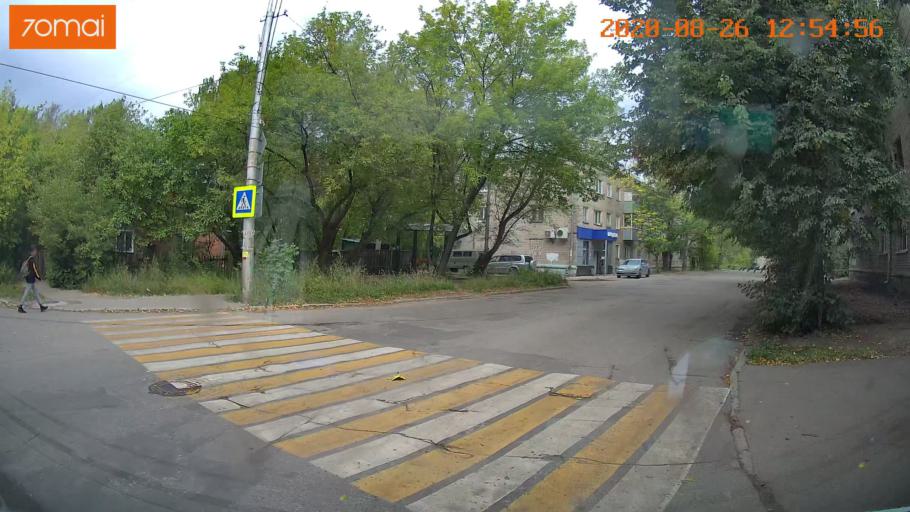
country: RU
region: Rjazan
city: Ryazan'
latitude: 54.6068
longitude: 39.7588
